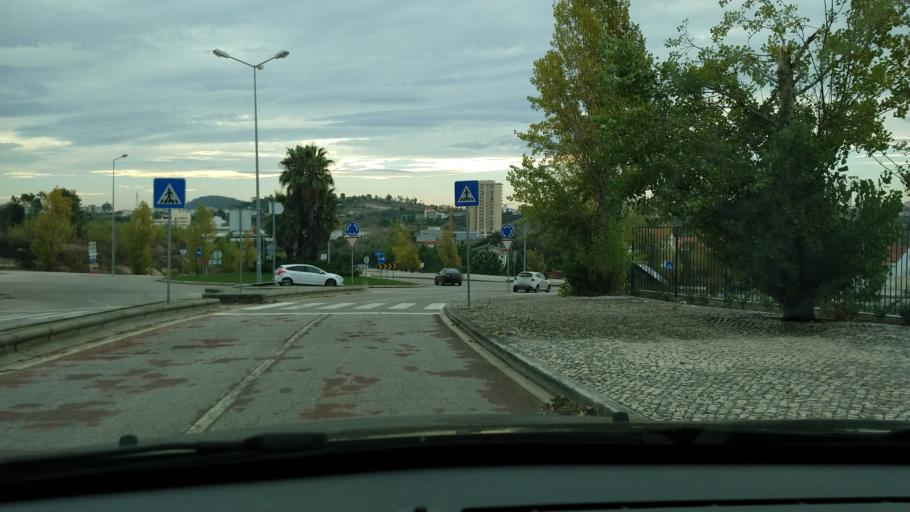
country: PT
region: Coimbra
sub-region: Figueira da Foz
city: Tavarede
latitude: 40.1580
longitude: -8.8501
